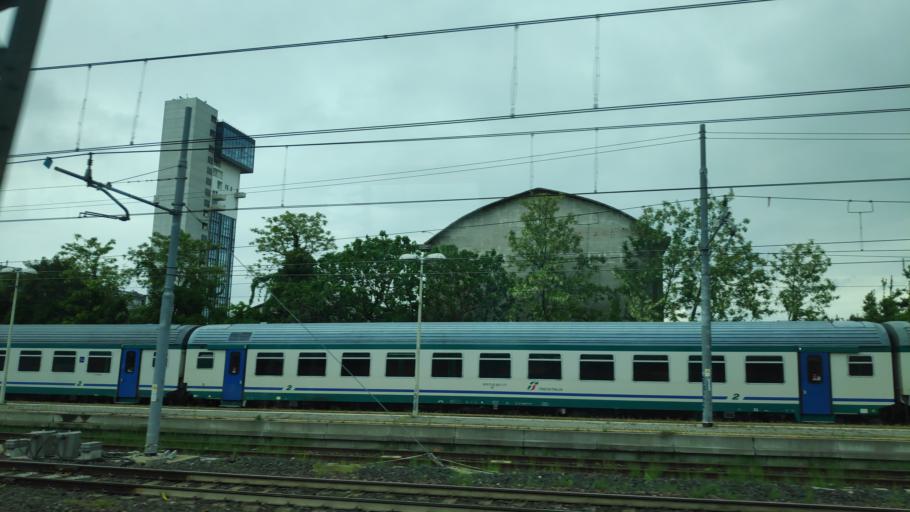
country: IT
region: Veneto
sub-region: Provincia di Venezia
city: Mestre
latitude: 45.4798
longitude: 12.2421
